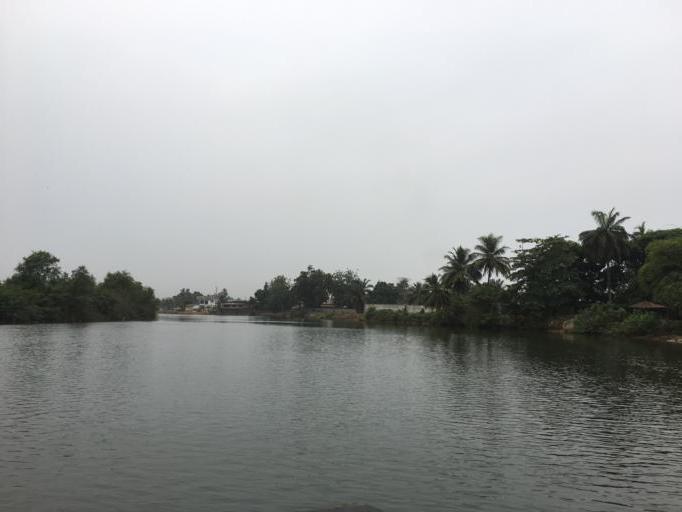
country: LR
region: Montserrado
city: Monrovia
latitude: 6.3792
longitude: -10.7810
